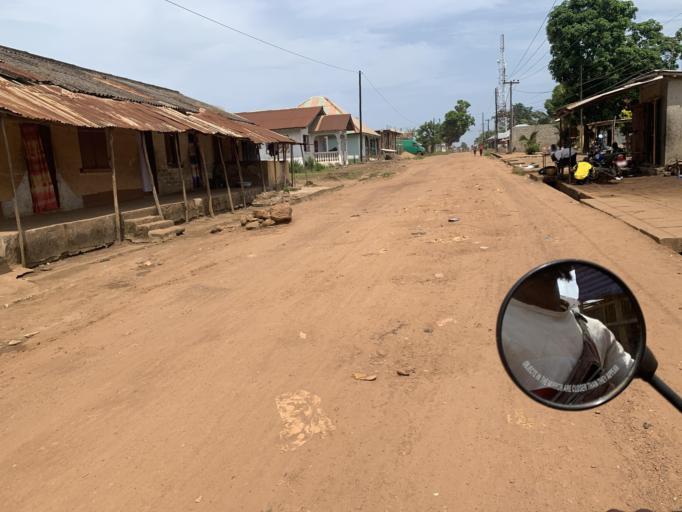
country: SL
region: Western Area
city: Hastings
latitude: 8.4066
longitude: -13.1339
